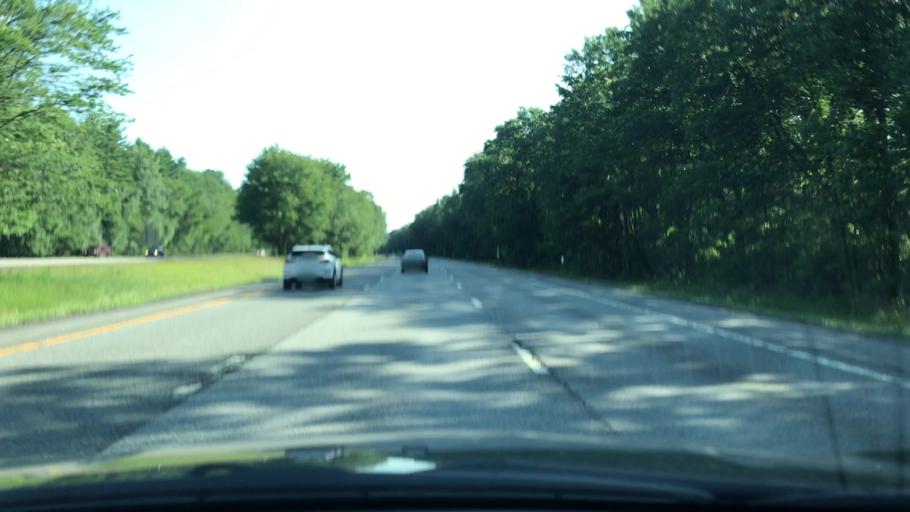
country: US
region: New York
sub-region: Saratoga County
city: Saratoga Springs
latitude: 43.1558
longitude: -73.7231
